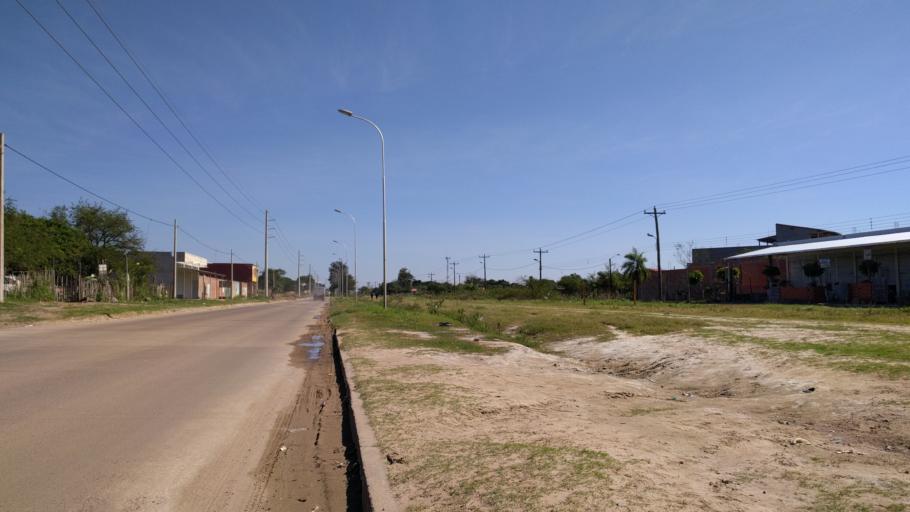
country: BO
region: Santa Cruz
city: Santa Cruz de la Sierra
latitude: -17.8696
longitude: -63.1973
